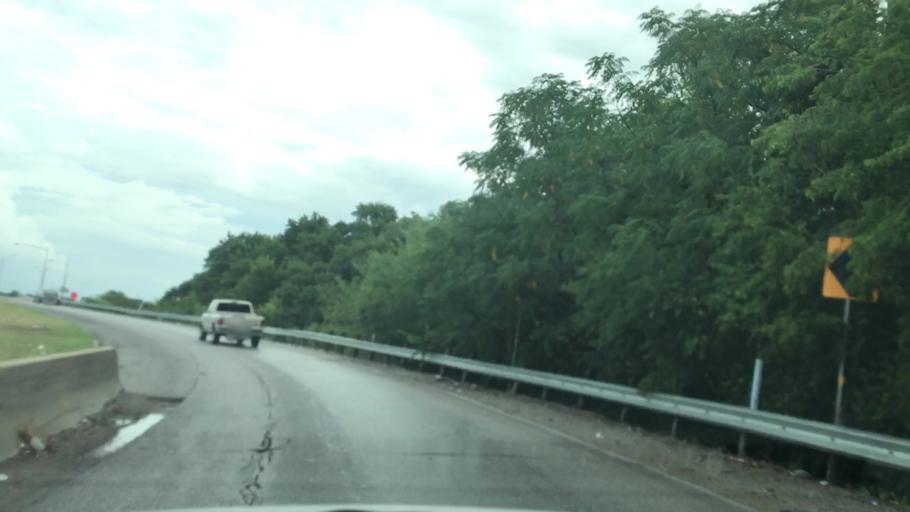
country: US
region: Texas
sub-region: Dallas County
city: Irving
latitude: 32.8444
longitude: -96.8782
